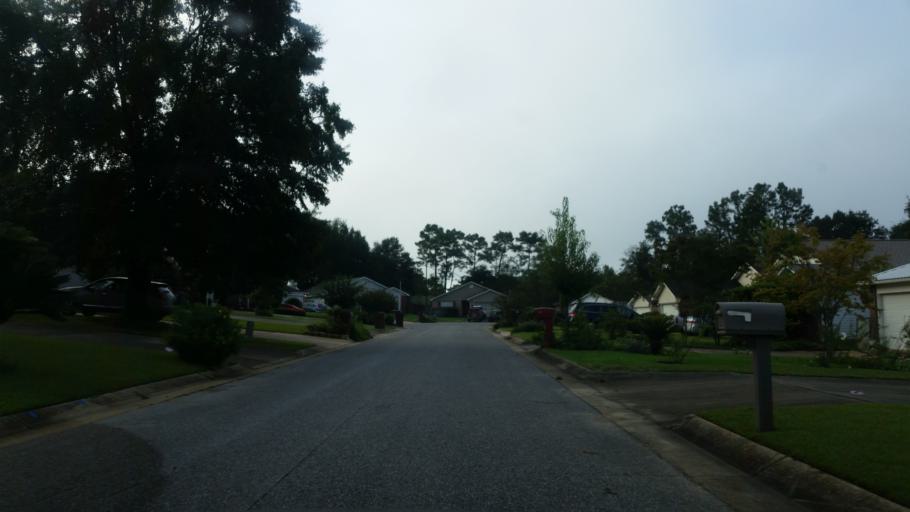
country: US
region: Florida
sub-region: Escambia County
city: Ferry Pass
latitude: 30.5044
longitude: -87.2030
